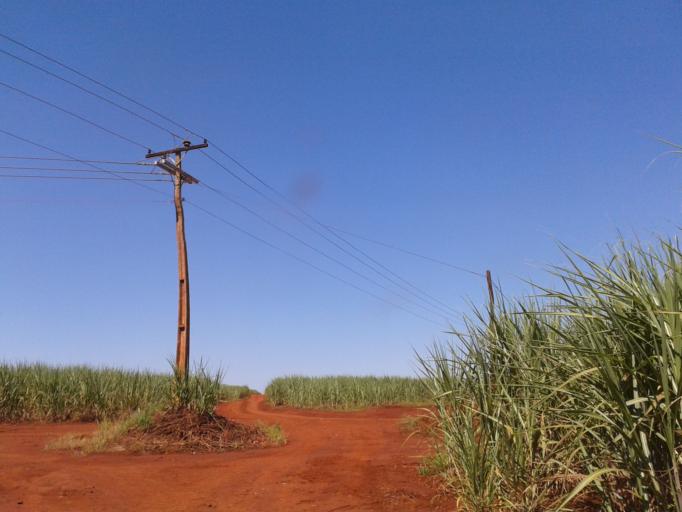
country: BR
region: Minas Gerais
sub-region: Centralina
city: Centralina
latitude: -18.6458
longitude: -49.2429
